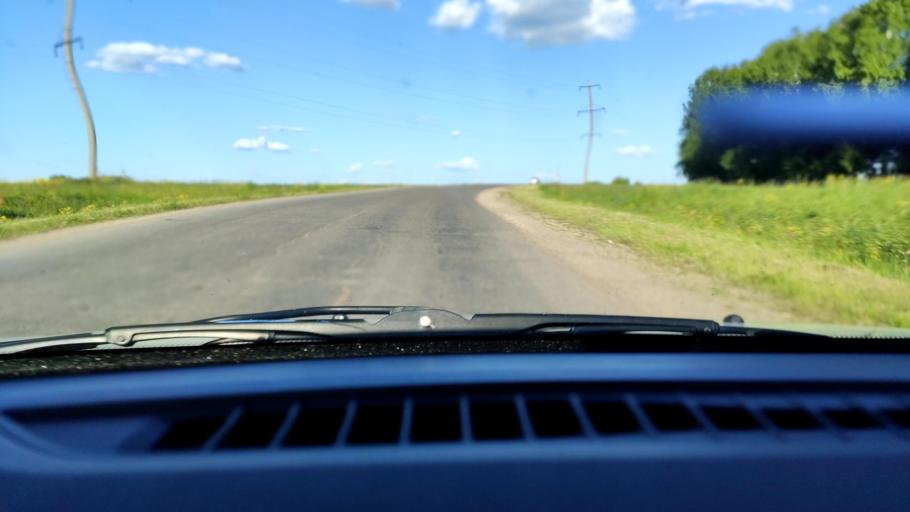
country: RU
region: Perm
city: Orda
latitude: 57.1906
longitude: 56.8618
